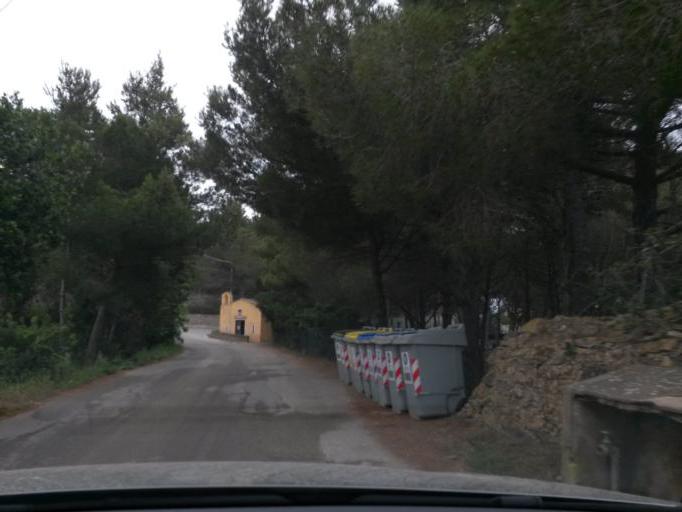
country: IT
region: Tuscany
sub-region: Provincia di Livorno
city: Capoliveri
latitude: 42.7496
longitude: 10.3689
